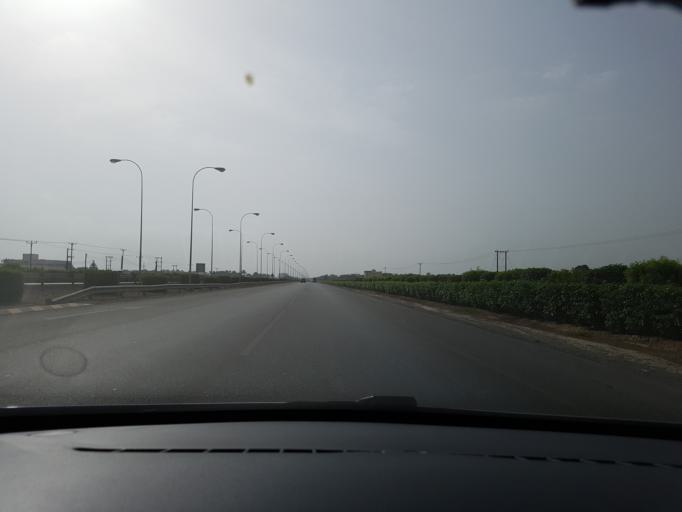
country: OM
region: Al Batinah
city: Al Sohar
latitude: 24.4056
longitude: 56.6538
